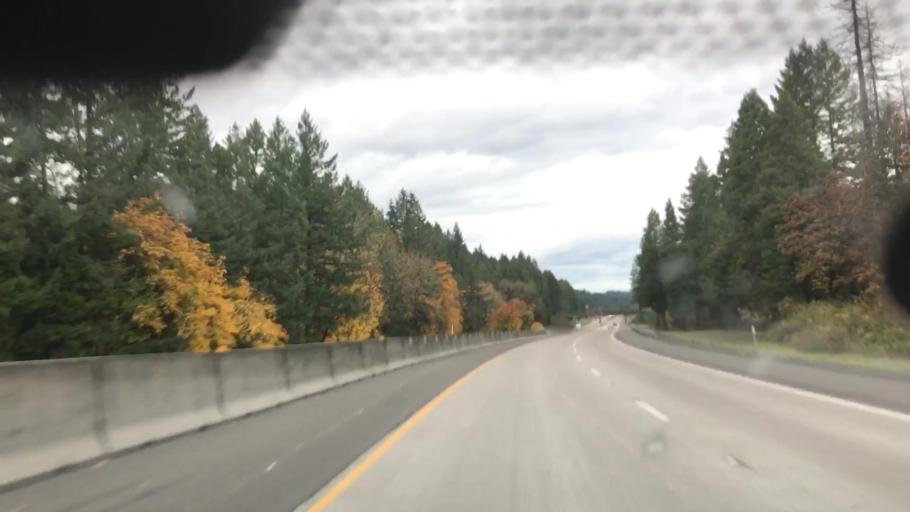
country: US
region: Oregon
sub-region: Douglas County
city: Yoncalla
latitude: 43.6311
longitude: -123.2194
